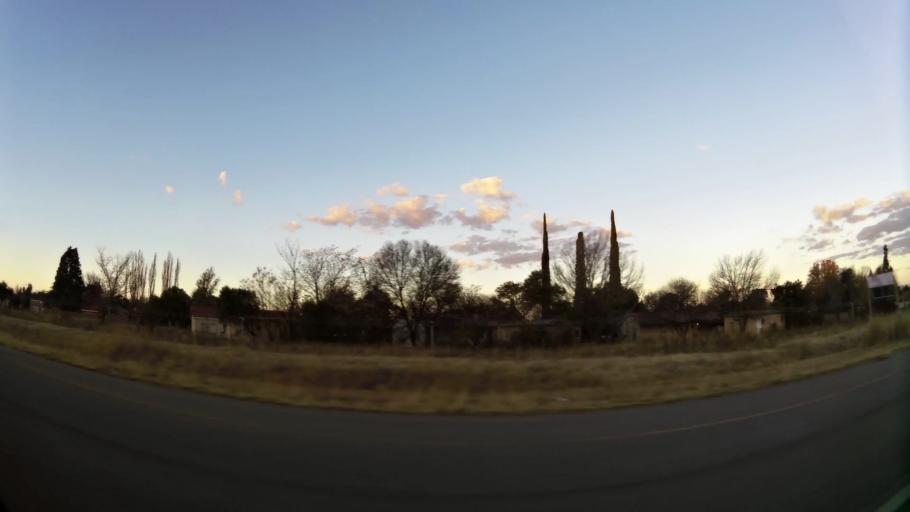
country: ZA
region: North-West
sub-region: Dr Kenneth Kaunda District Municipality
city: Potchefstroom
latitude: -26.6840
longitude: 27.0761
